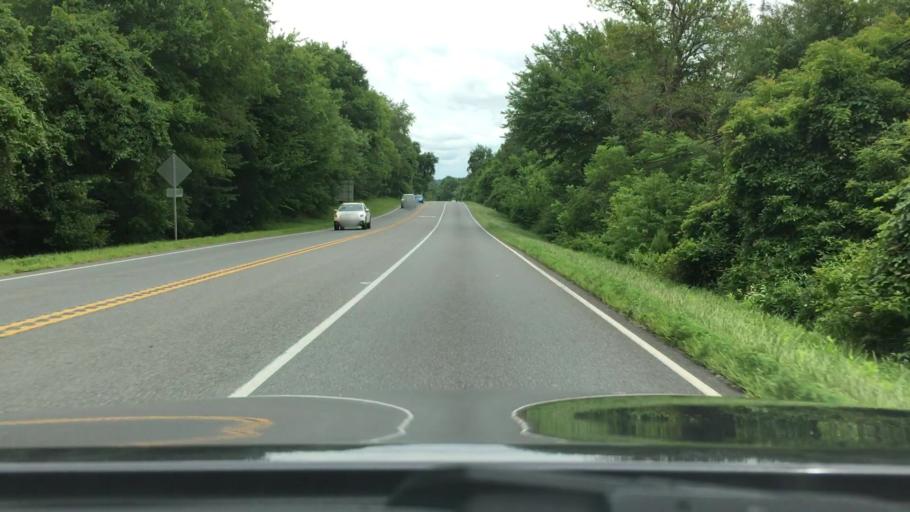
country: US
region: Virginia
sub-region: City of Charlottesville
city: Charlottesville
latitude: 38.0159
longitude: -78.4217
